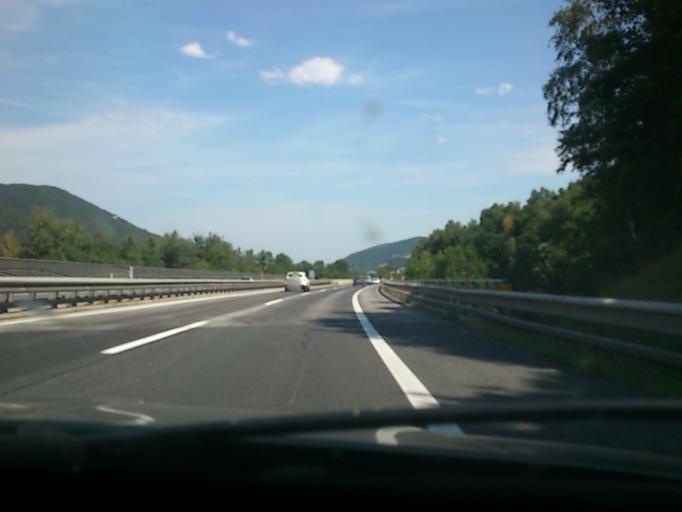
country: AT
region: Lower Austria
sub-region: Politischer Bezirk Neunkirchen
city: Grimmenstein
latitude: 47.6103
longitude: 16.1289
